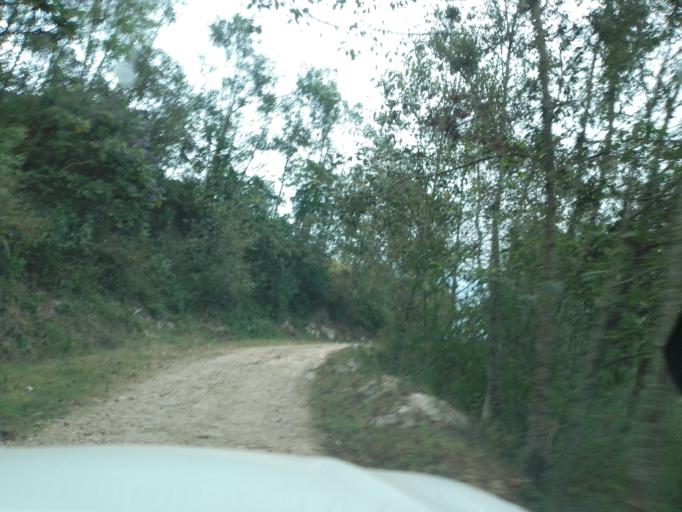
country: MX
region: Chiapas
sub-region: Cacahoatan
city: Benito Juarez
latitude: 15.2082
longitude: -92.2223
